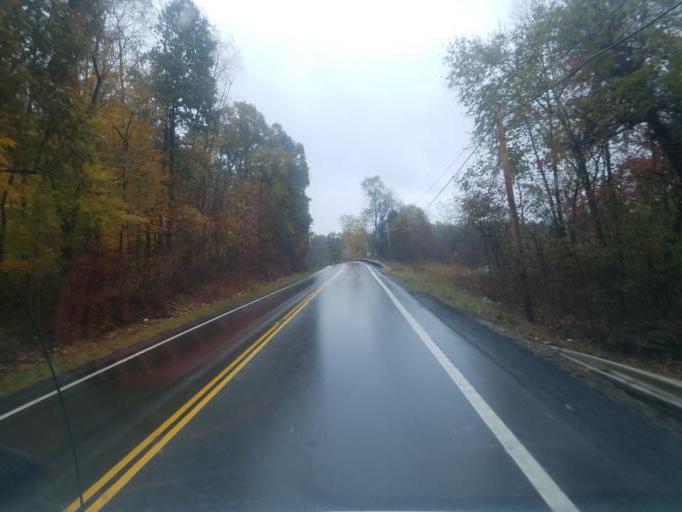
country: US
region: Ohio
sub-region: Muskingum County
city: Frazeysburg
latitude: 40.1172
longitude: -82.1852
